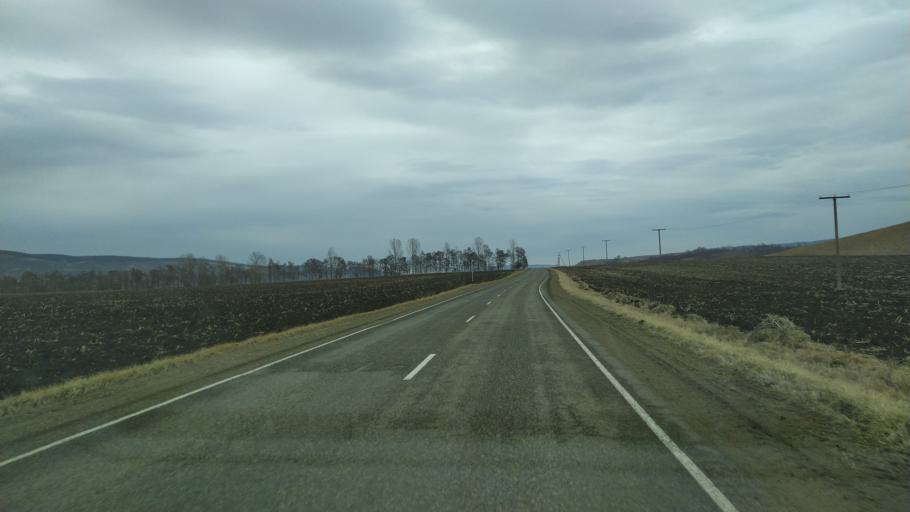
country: RU
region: Krasnodarskiy
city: Peredovaya
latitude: 44.0962
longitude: 41.3946
